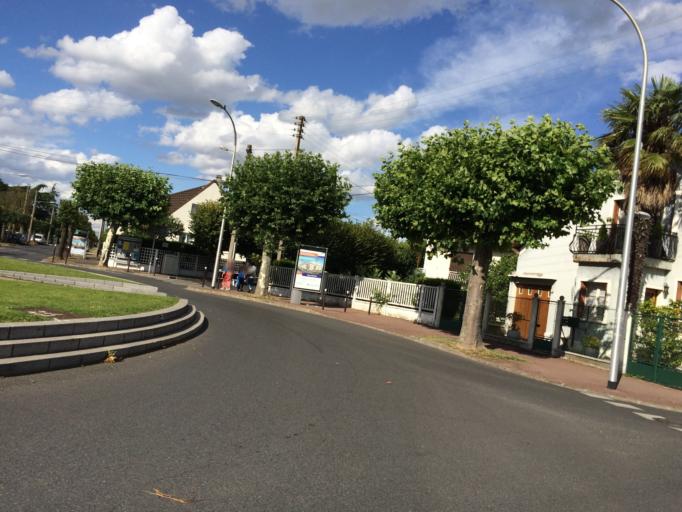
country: FR
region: Ile-de-France
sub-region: Departement de l'Essonne
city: Paray-Vieille-Poste
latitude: 48.7091
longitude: 2.3590
